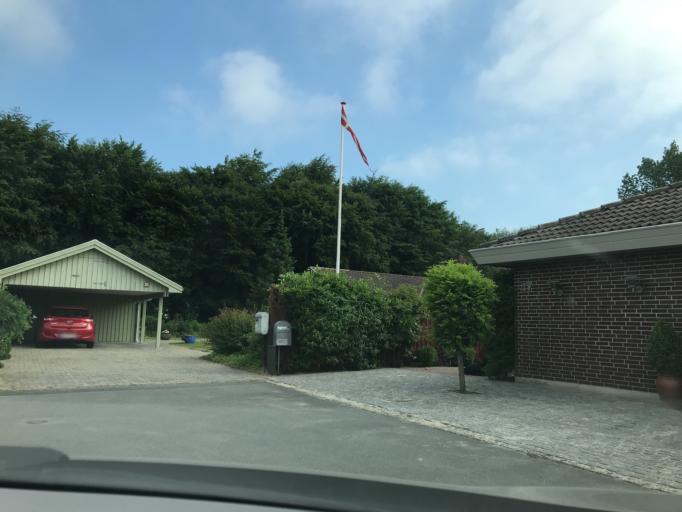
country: DK
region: South Denmark
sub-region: Odense Kommune
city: Bellinge
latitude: 55.3758
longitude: 10.3438
